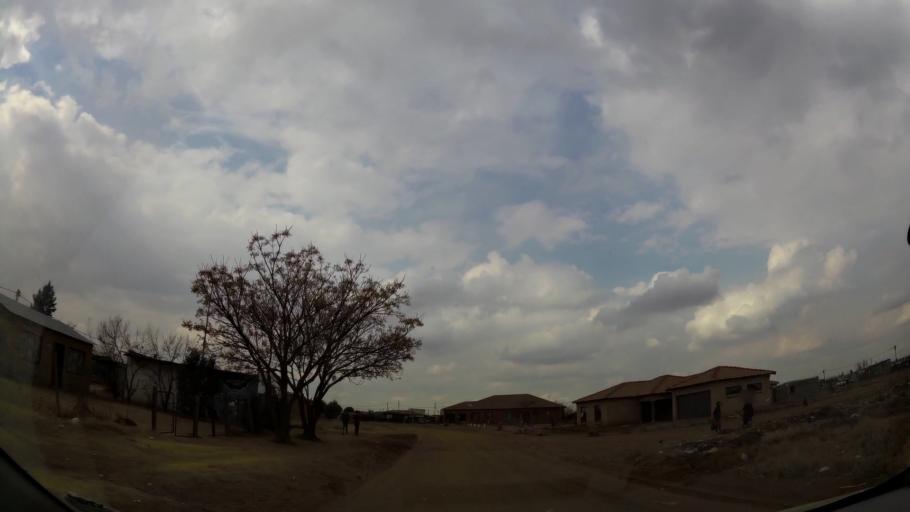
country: ZA
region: Orange Free State
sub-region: Fezile Dabi District Municipality
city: Sasolburg
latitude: -26.8635
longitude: 27.8785
